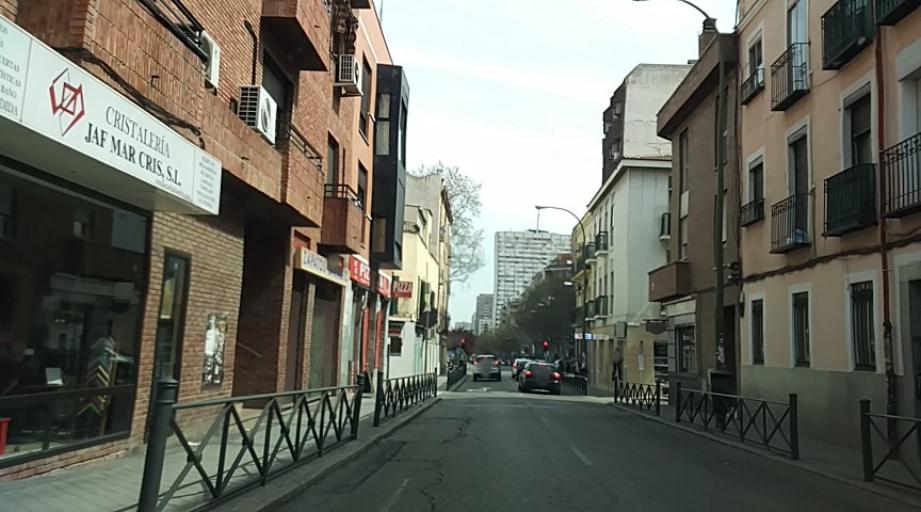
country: ES
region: Madrid
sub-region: Provincia de Madrid
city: Chamberi
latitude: 40.4527
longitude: -3.7004
